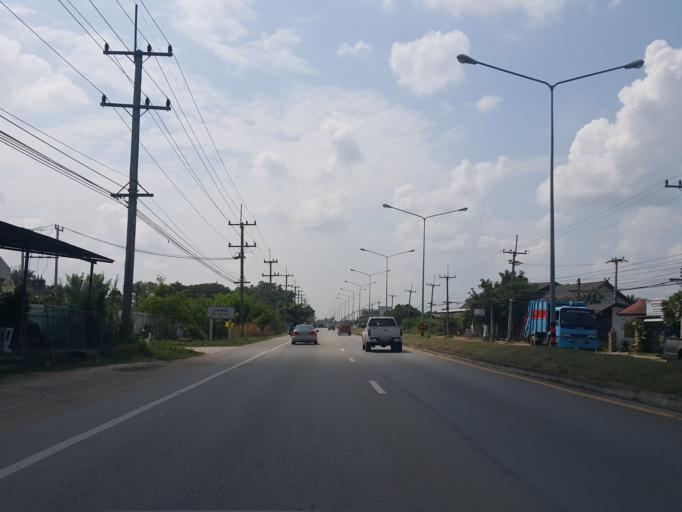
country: TH
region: Lamphun
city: Pa Sang
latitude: 18.5219
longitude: 98.8492
